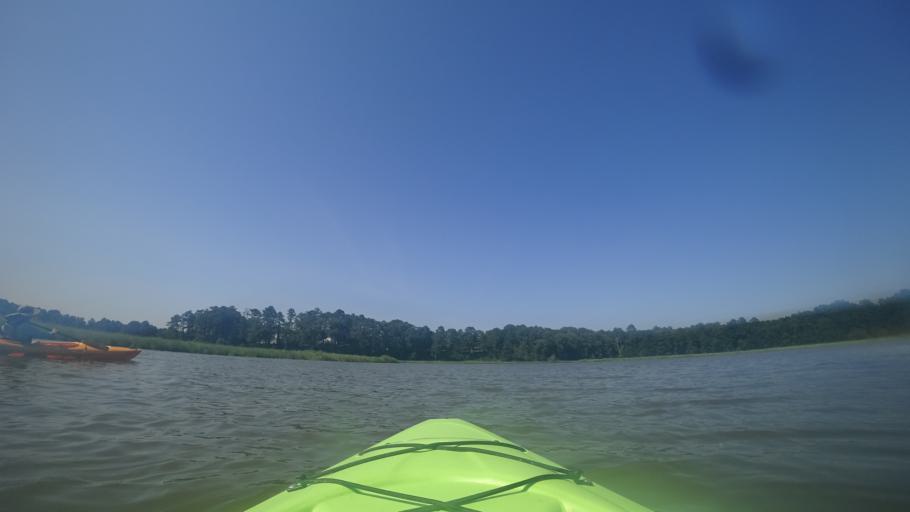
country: US
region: Virginia
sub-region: Isle of Wight County
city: Smithfield
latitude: 36.9587
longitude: -76.6147
